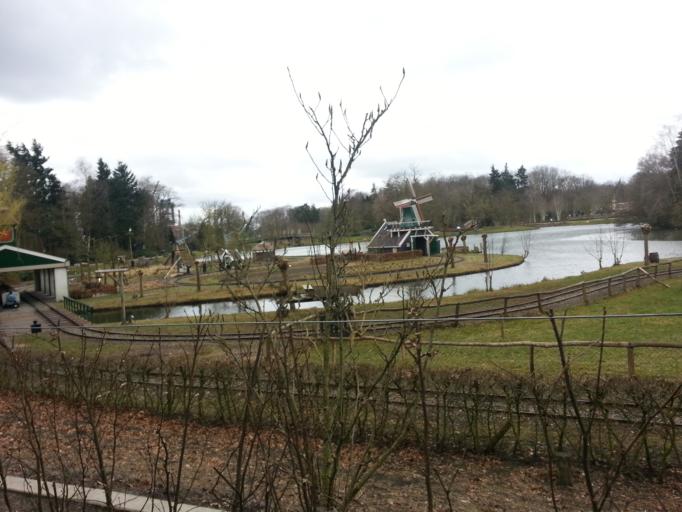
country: NL
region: North Brabant
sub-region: Gemeente Loon op Zand
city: Loon op Zand
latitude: 51.6502
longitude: 5.0537
